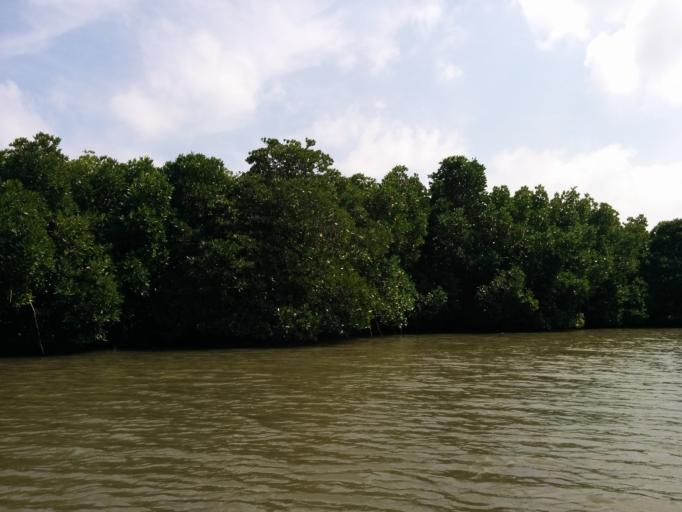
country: IN
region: Tamil Nadu
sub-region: Cuddalore
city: Annamalainagar
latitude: 11.4292
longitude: 79.7934
